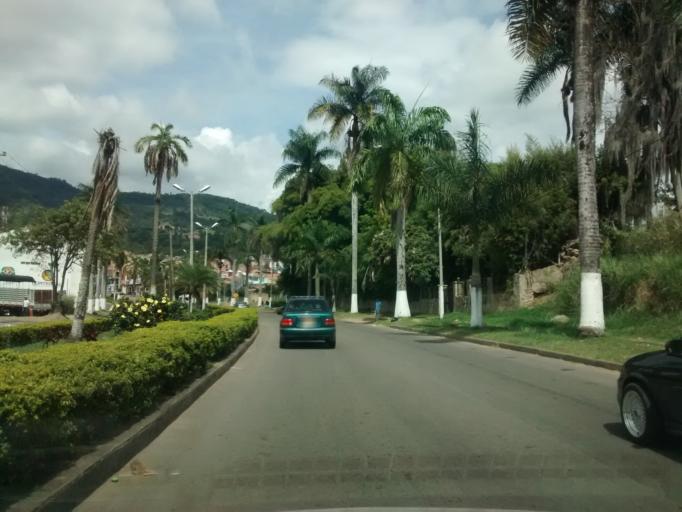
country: CO
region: Cundinamarca
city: Fusagasuga
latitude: 4.3417
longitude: -74.3682
